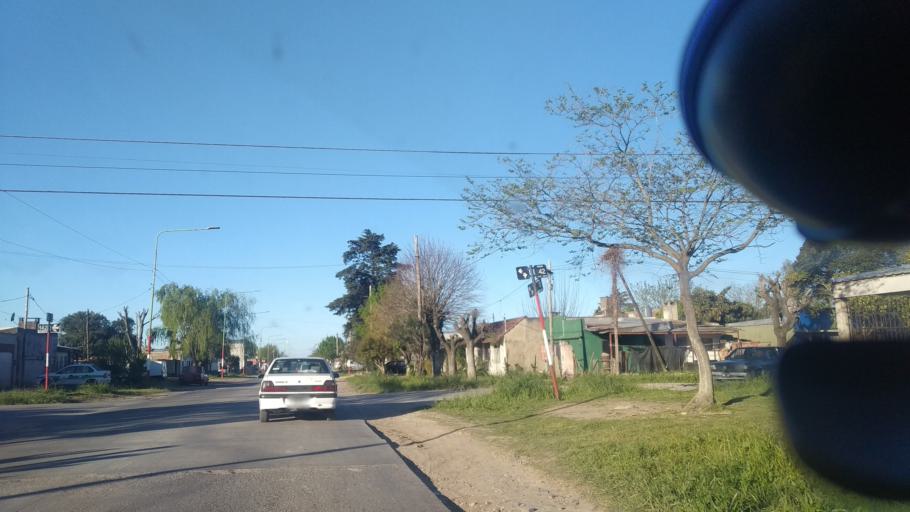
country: AR
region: Buenos Aires
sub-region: Partido de La Plata
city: La Plata
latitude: -34.9644
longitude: -57.9645
